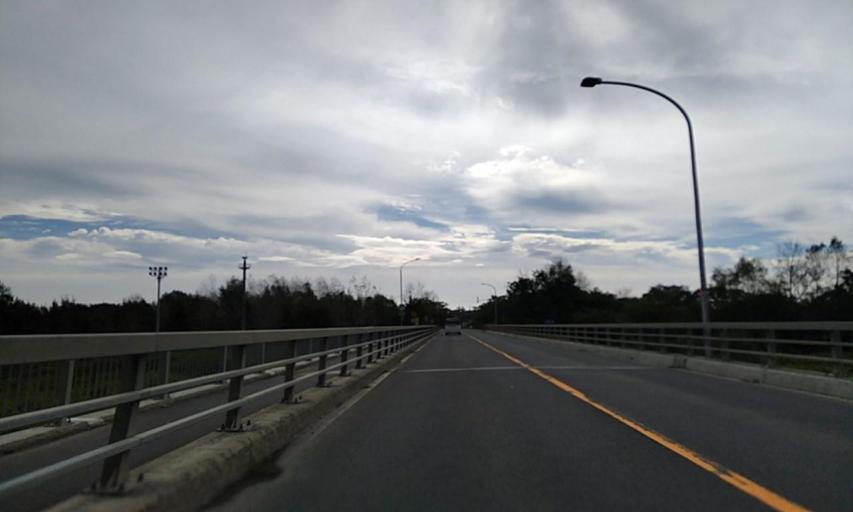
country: JP
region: Hokkaido
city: Obihiro
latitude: 42.8403
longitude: 143.1866
